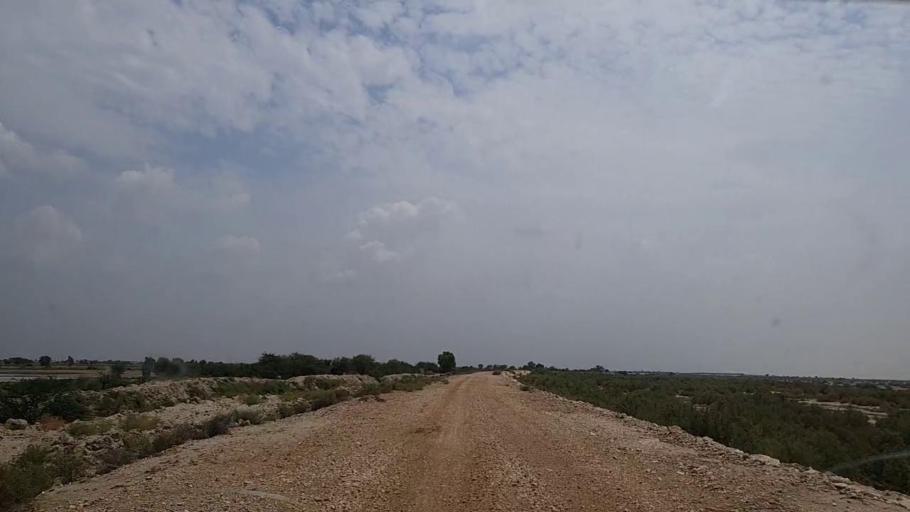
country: PK
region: Sindh
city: Phulji
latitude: 26.8328
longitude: 67.6174
